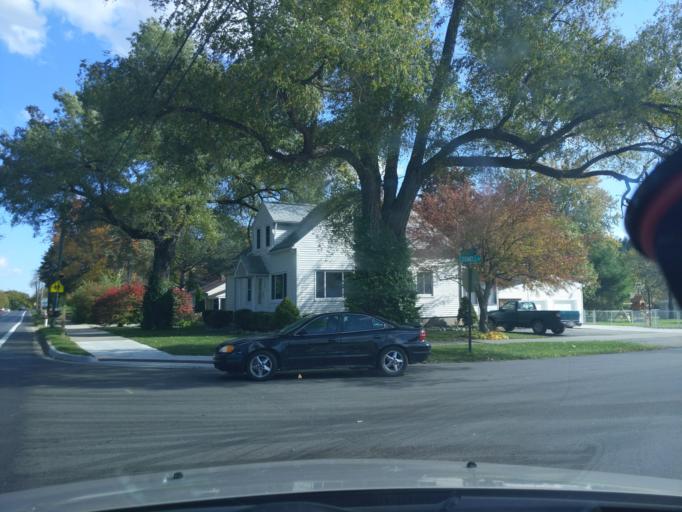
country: US
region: Michigan
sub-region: Ingham County
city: Haslett
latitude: 42.7467
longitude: -84.3932
